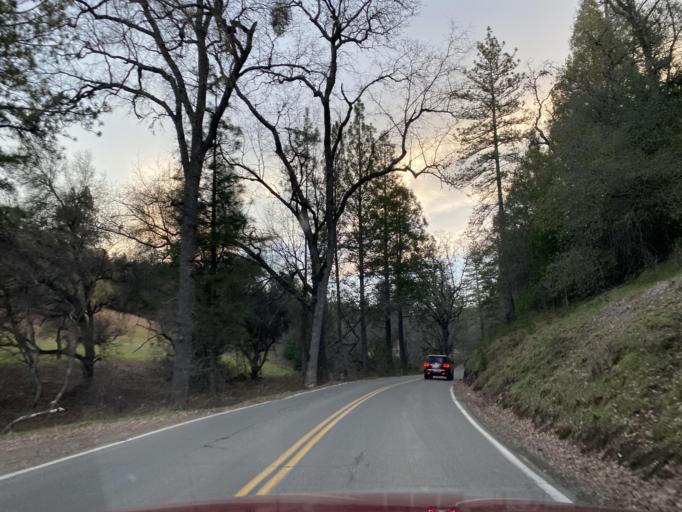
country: US
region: California
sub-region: Amador County
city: Pine Grove
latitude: 38.4987
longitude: -120.7117
